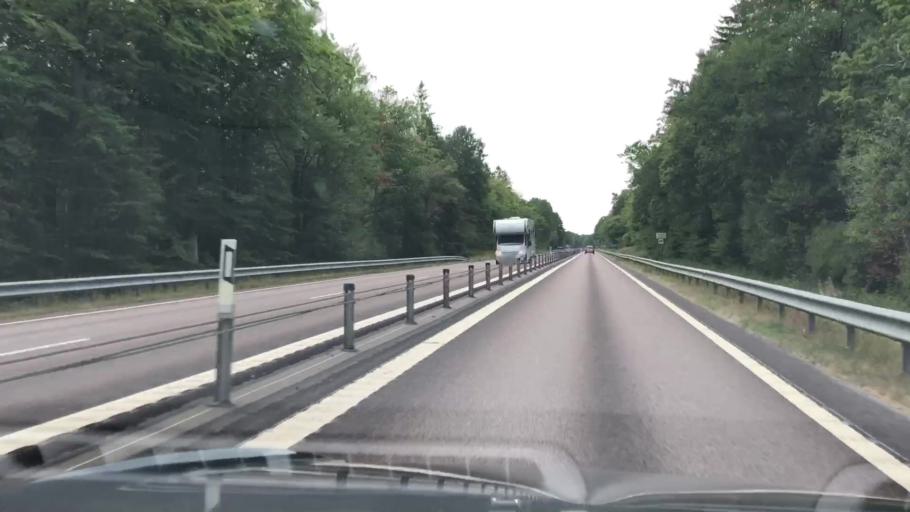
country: SE
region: Blekinge
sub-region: Karlskrona Kommun
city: Jaemjoe
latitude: 56.2347
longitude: 15.9206
